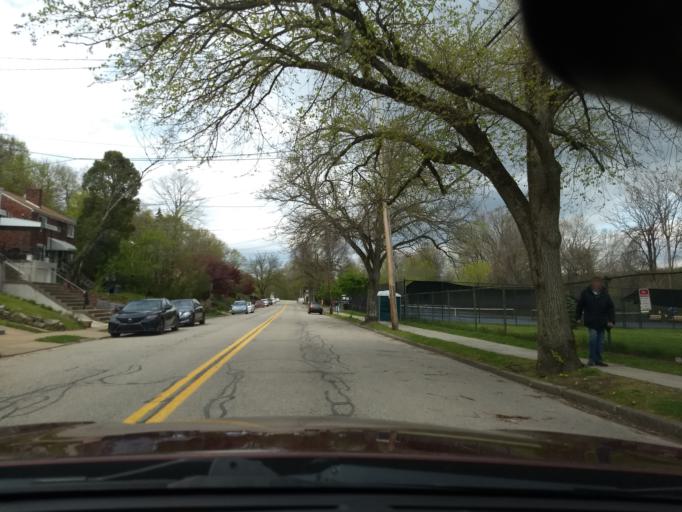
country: US
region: Pennsylvania
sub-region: Allegheny County
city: Aspinwall
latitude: 40.4731
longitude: -79.9111
